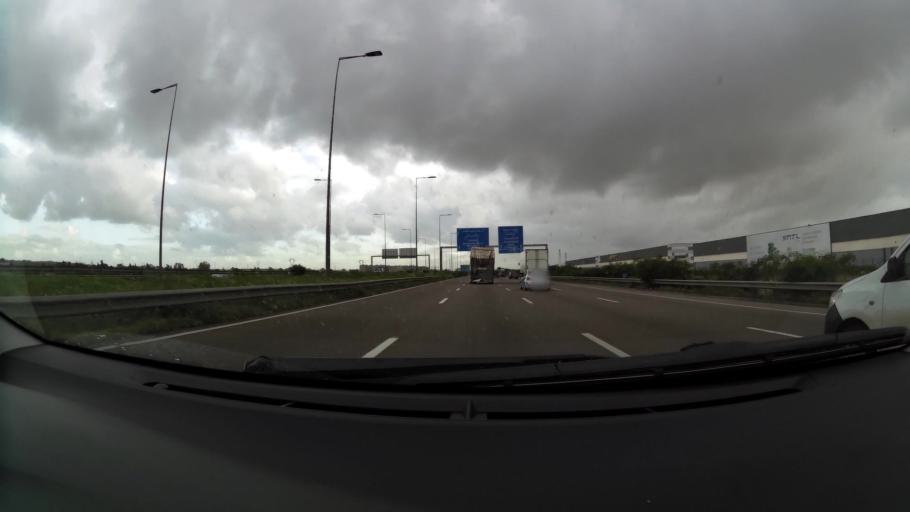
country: MA
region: Grand Casablanca
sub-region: Mohammedia
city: Mohammedia
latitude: 33.6575
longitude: -7.4095
